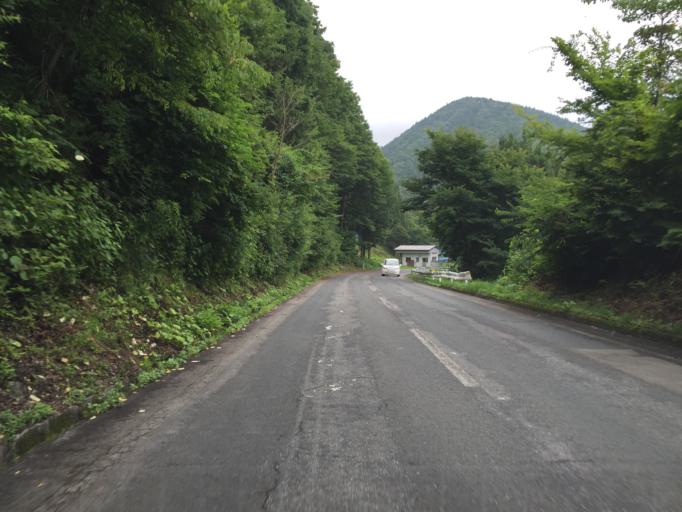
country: JP
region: Fukushima
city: Inawashiro
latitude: 37.6569
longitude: 140.1599
